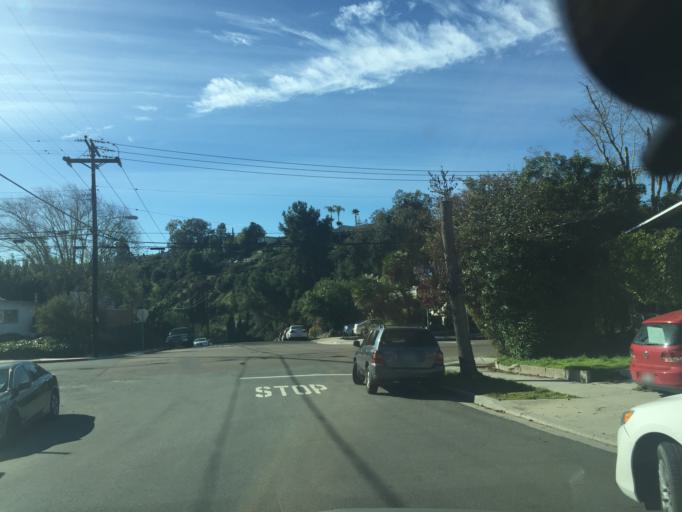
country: US
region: California
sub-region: San Diego County
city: Lemon Grove
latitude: 32.7681
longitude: -117.0797
